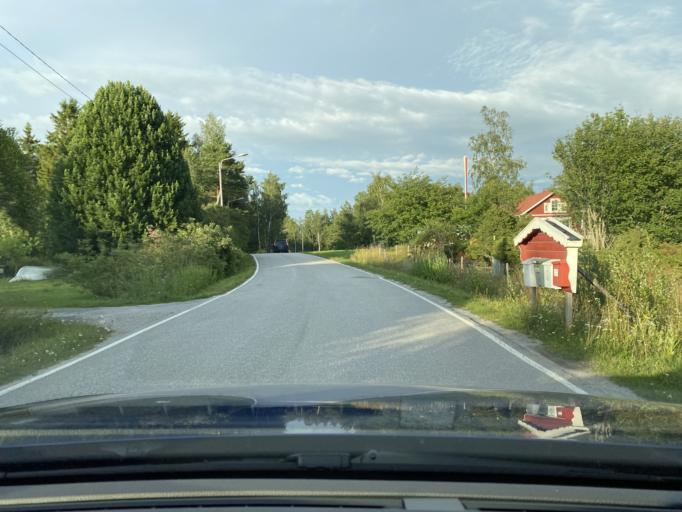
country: FI
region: Ostrobothnia
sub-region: Vaasa
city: Korsnaes
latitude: 62.9728
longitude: 21.1651
